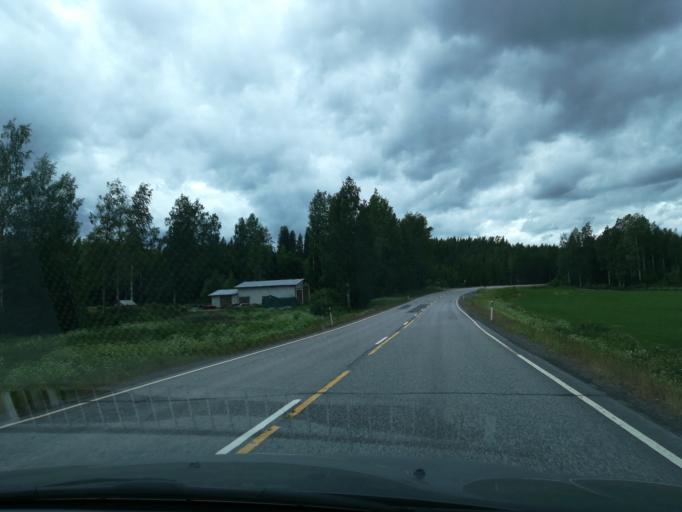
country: FI
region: South Karelia
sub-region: Lappeenranta
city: Lemi
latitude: 61.1134
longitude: 27.8656
